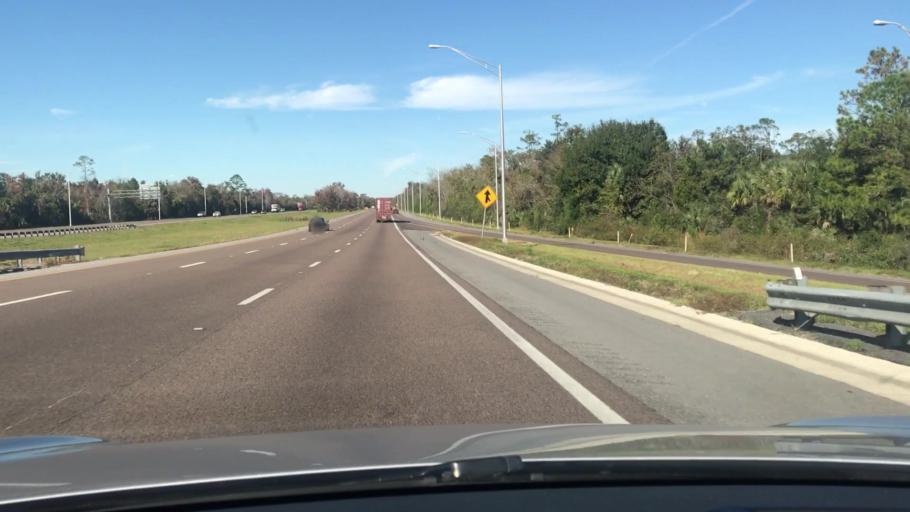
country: US
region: Florida
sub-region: Volusia County
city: Edgewater
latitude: 28.9531
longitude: -80.9514
